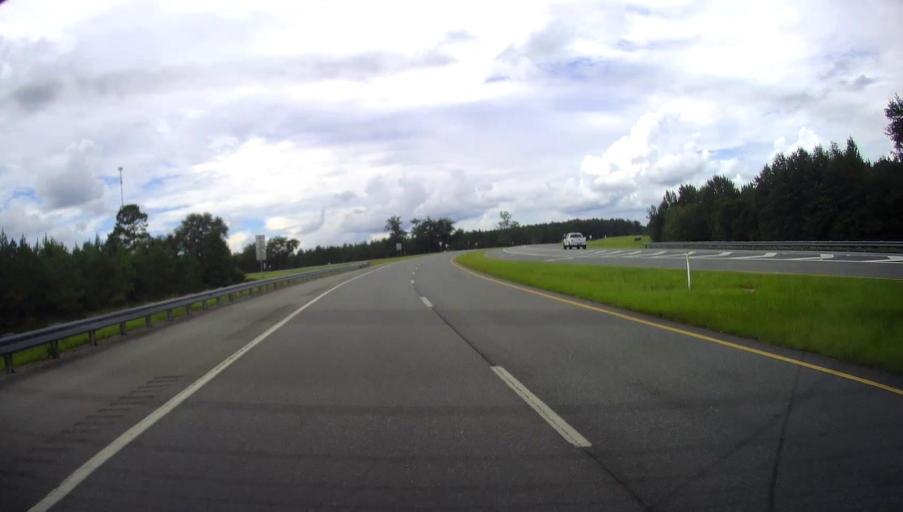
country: US
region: Georgia
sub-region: Schley County
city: Ellaville
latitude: 32.2540
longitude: -84.3016
